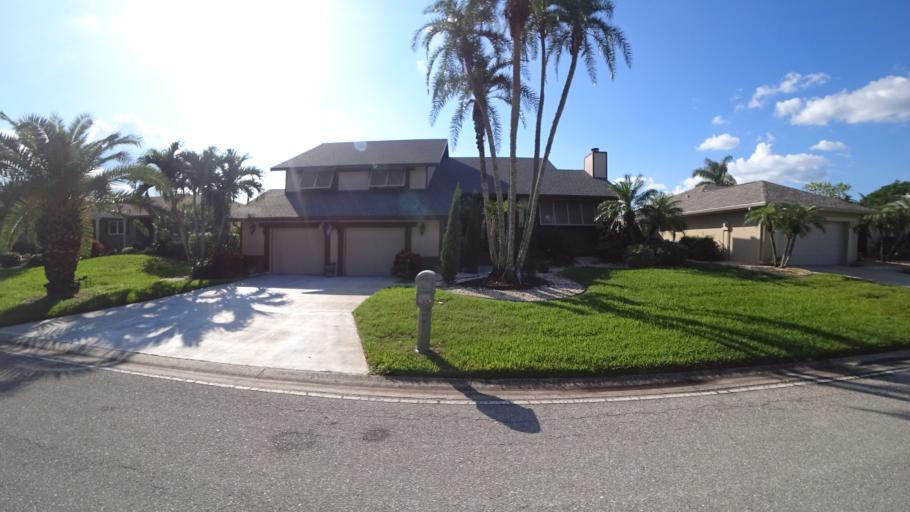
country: US
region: Florida
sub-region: Manatee County
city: Longboat Key
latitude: 27.4519
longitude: -82.6486
